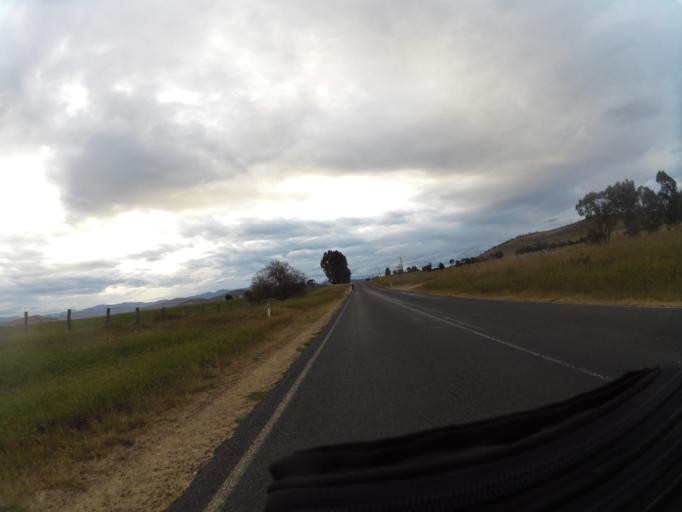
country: AU
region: New South Wales
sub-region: Greater Hume Shire
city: Holbrook
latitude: -36.0671
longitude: 147.9547
